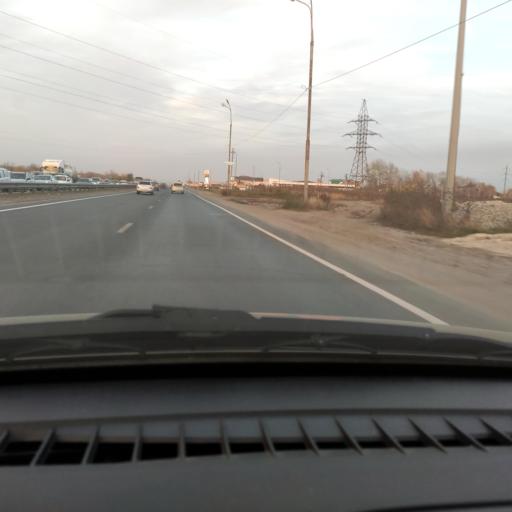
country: RU
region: Samara
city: Tol'yatti
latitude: 53.5616
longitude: 49.3614
